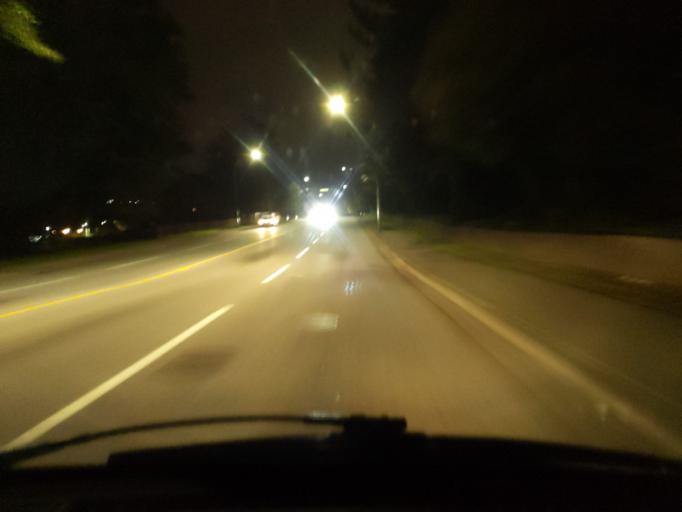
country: CA
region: British Columbia
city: Burnaby
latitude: 49.2546
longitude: -123.0170
